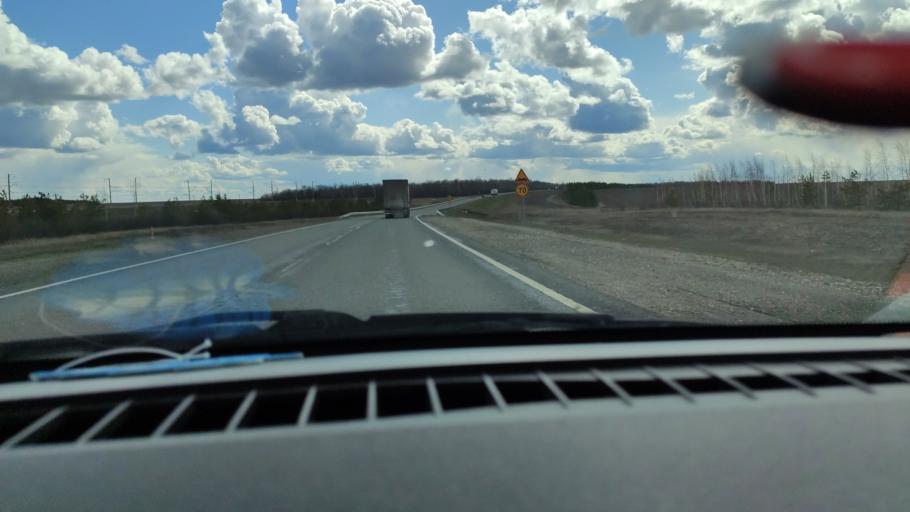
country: RU
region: Samara
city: Syzran'
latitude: 52.8731
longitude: 48.2871
